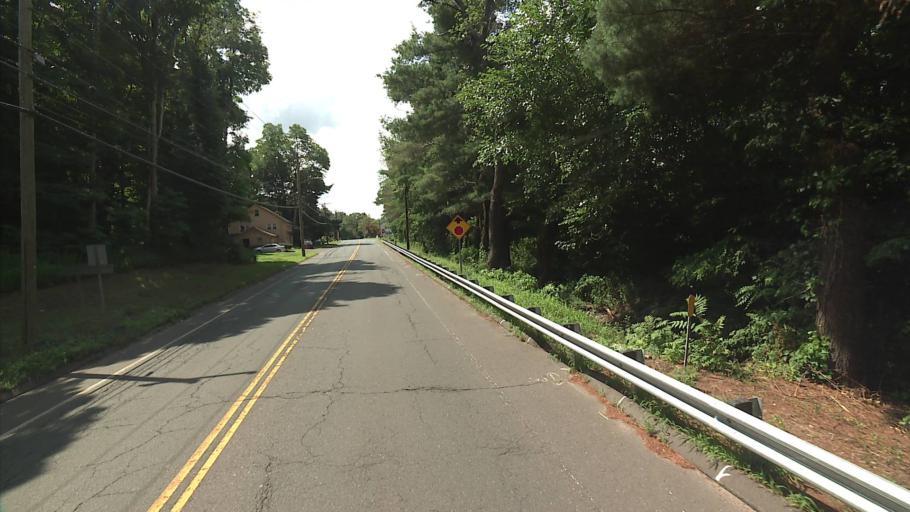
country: US
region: Connecticut
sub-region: Middlesex County
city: Cromwell
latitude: 41.6035
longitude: -72.6037
